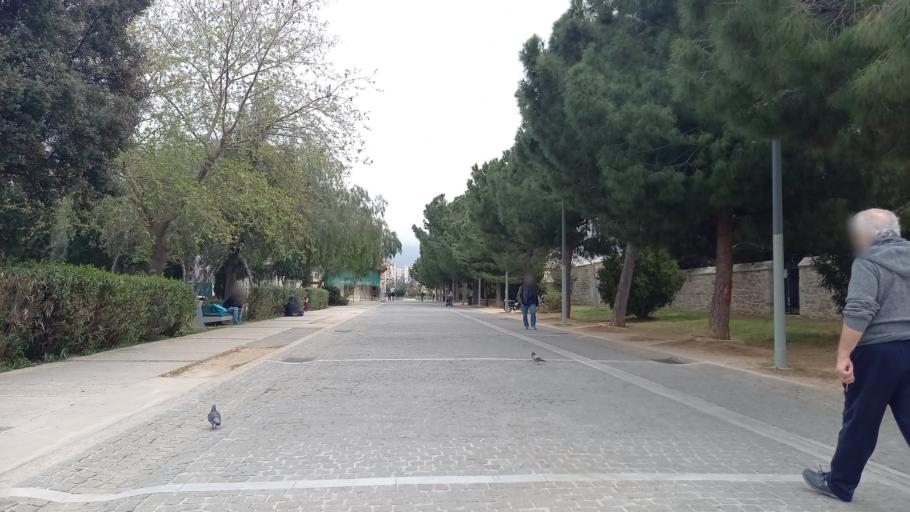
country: GR
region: Attica
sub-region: Nomarchia Athinas
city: Athens
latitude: 37.9777
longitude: 23.7188
